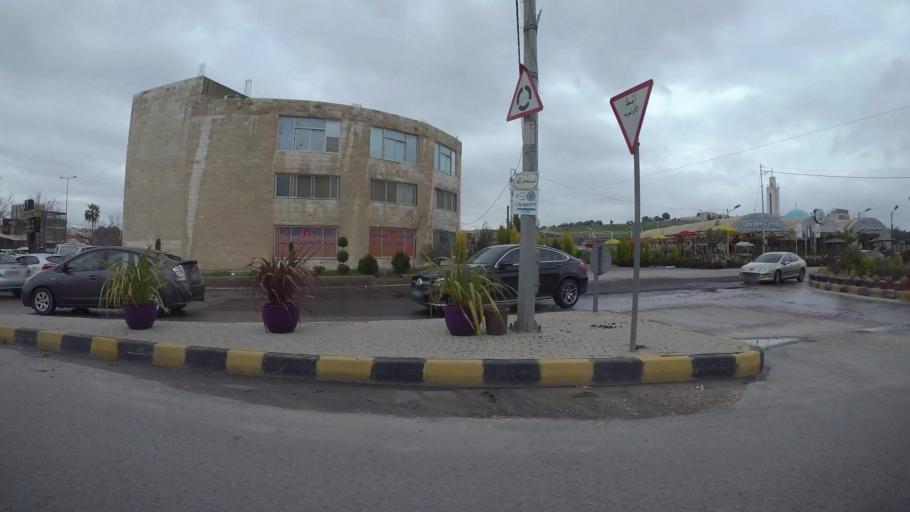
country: JO
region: Amman
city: Wadi as Sir
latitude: 31.9747
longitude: 35.8410
